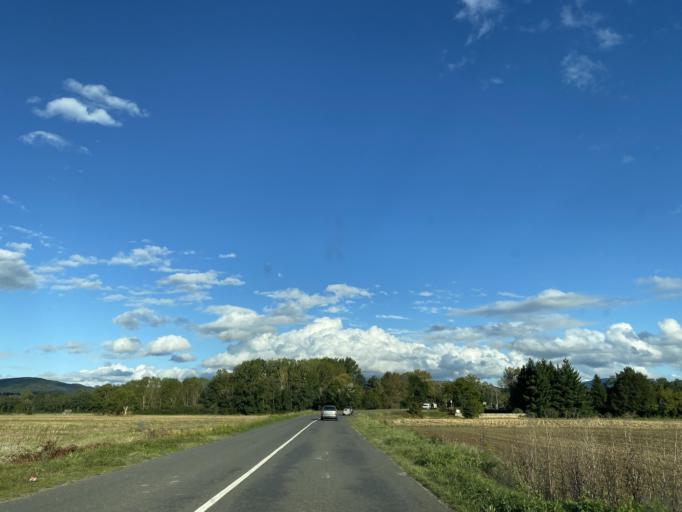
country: FR
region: Auvergne
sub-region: Departement du Puy-de-Dome
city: Puy-Guillaume
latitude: 45.9635
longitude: 3.4598
